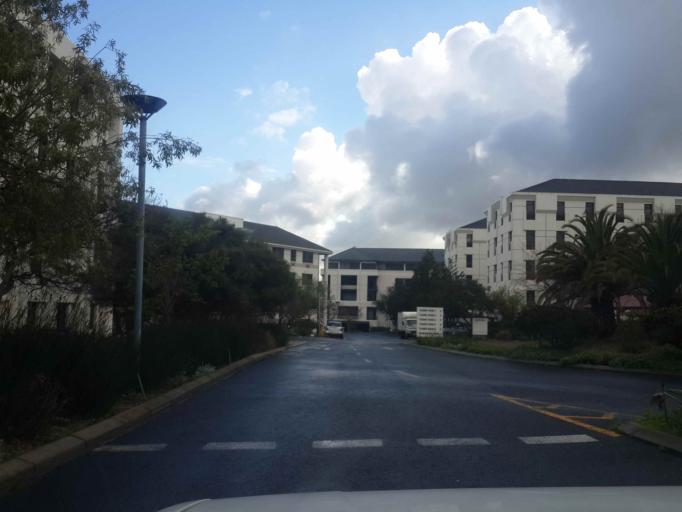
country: ZA
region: Western Cape
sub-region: City of Cape Town
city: Kraaifontein
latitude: -33.8800
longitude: 18.6354
